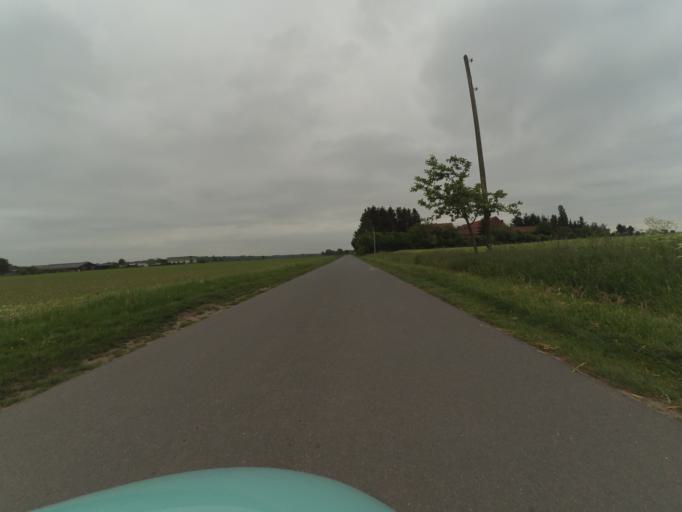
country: DE
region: Lower Saxony
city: Haenigsen
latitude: 52.4807
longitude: 10.1048
